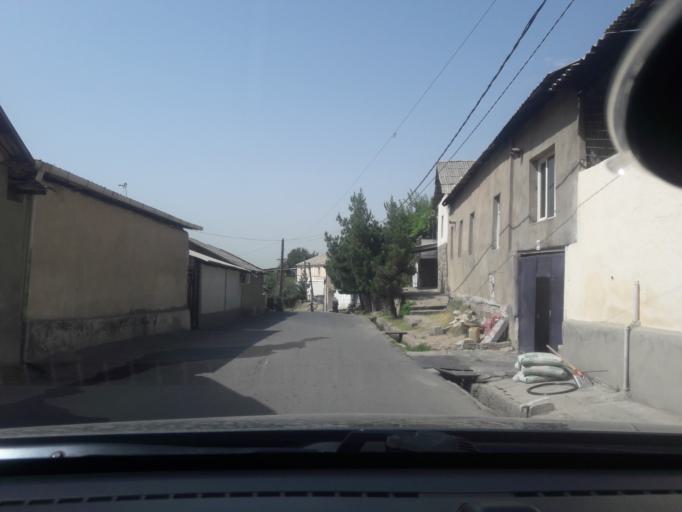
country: TJ
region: Dushanbe
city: Dushanbe
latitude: 38.5984
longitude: 68.7973
